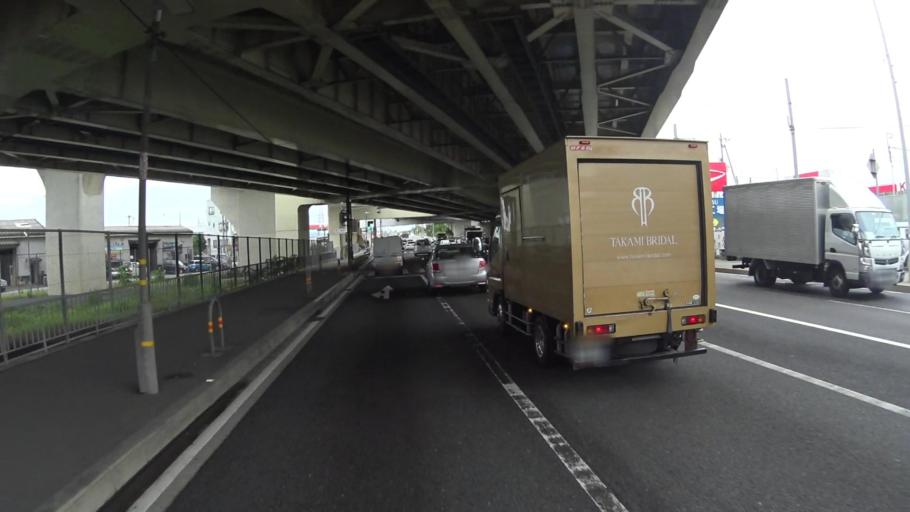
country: JP
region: Kyoto
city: Yawata
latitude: 34.9059
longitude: 135.6985
